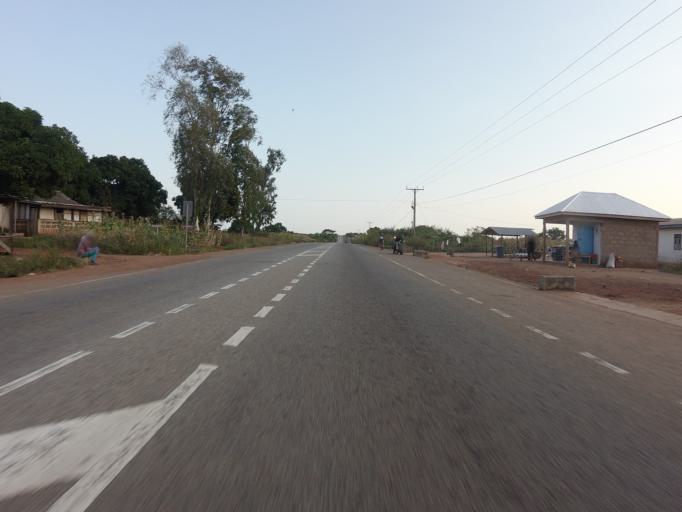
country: GH
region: Volta
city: Anloga
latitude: 6.0497
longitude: 0.6046
